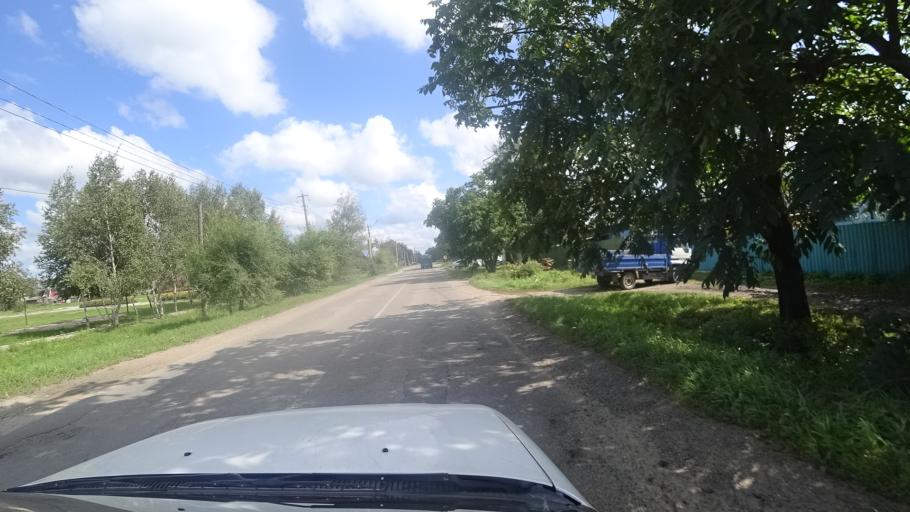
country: RU
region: Primorskiy
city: Dal'nerechensk
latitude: 45.9297
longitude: 133.7622
